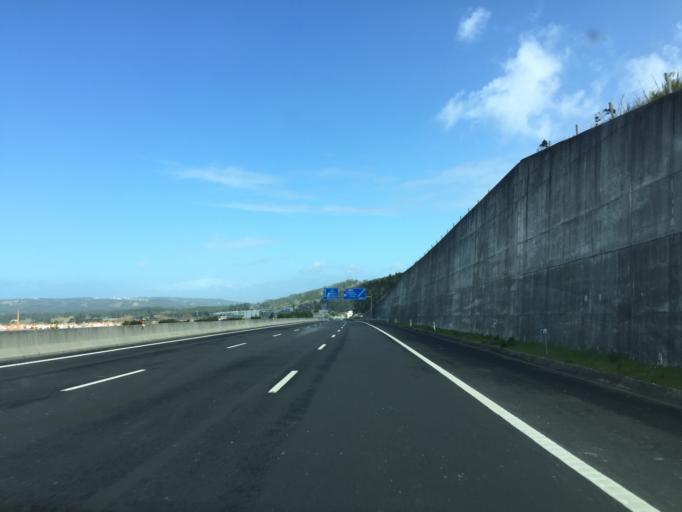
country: PT
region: Leiria
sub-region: Caldas da Rainha
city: Caldas da Rainha
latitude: 39.4896
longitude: -9.0950
